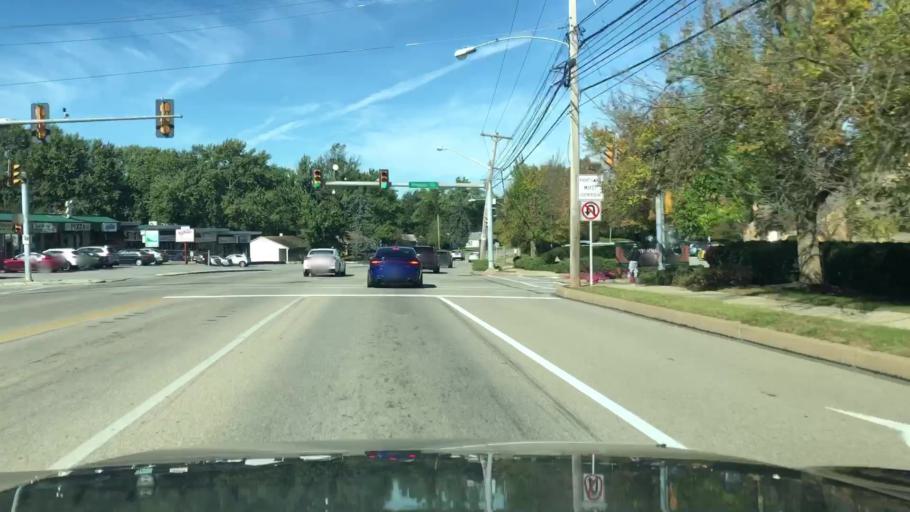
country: US
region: Pennsylvania
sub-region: Montgomery County
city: Plymouth Meeting
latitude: 40.1285
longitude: -75.2990
